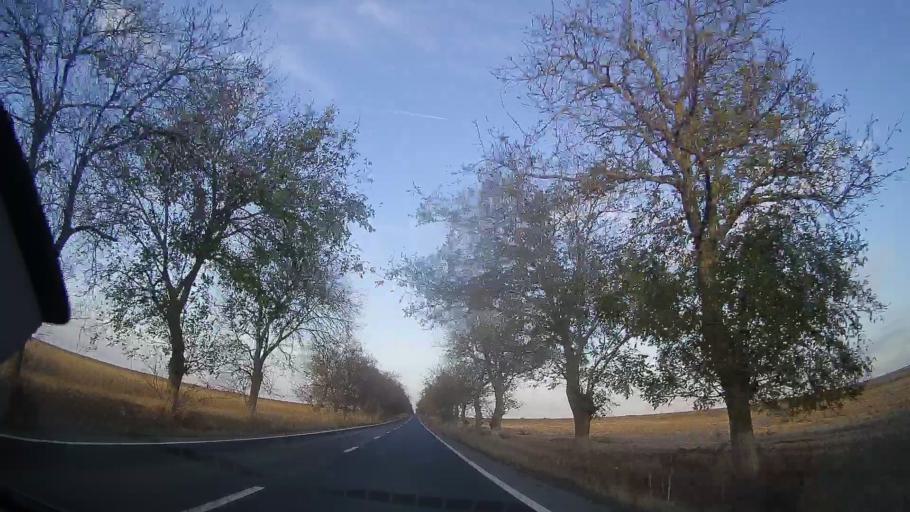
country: RO
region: Constanta
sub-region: Comuna Chirnogeni
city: Chirnogeni
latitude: 43.8519
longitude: 28.2440
